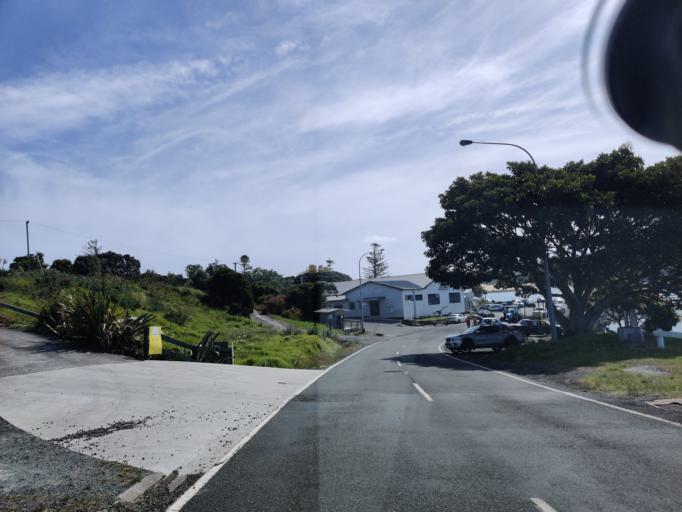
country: NZ
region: Northland
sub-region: Far North District
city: Ahipara
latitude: -35.5043
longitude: 173.3934
